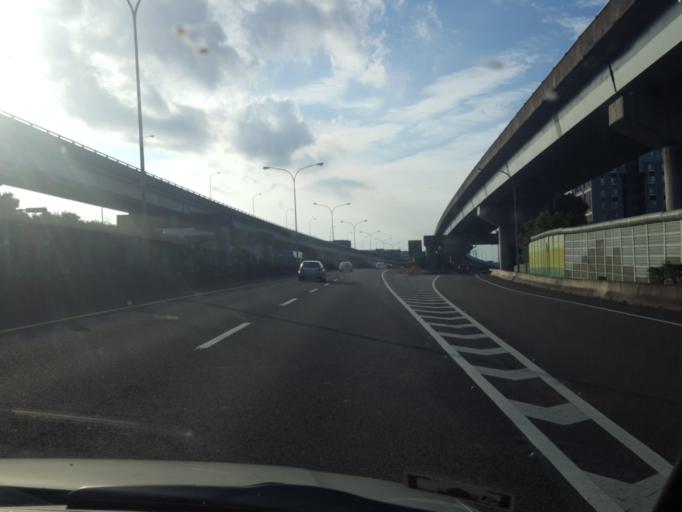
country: TW
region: Taipei
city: Taipei
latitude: 25.0640
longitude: 121.5944
